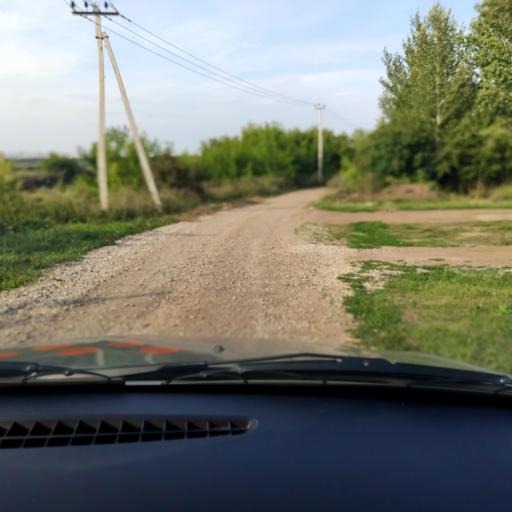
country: RU
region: Bashkortostan
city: Ufa
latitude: 54.6084
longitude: 55.9527
